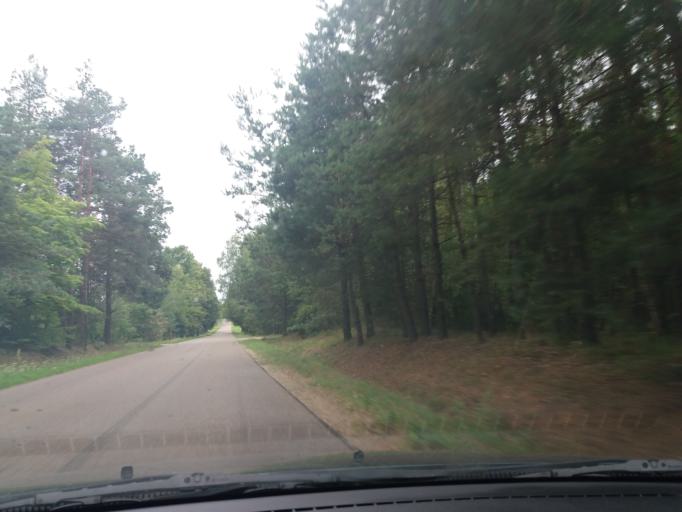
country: PL
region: Masovian Voivodeship
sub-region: Powiat mlawski
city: Wieczfnia Koscielna
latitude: 53.2044
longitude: 20.4951
